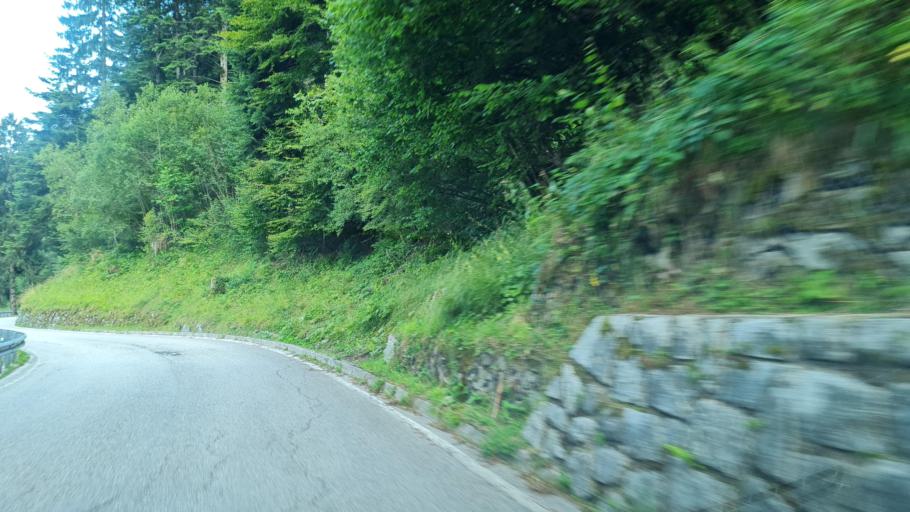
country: IT
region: Trentino-Alto Adige
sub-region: Provincia di Trento
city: Telve
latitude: 46.1204
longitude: 11.4837
